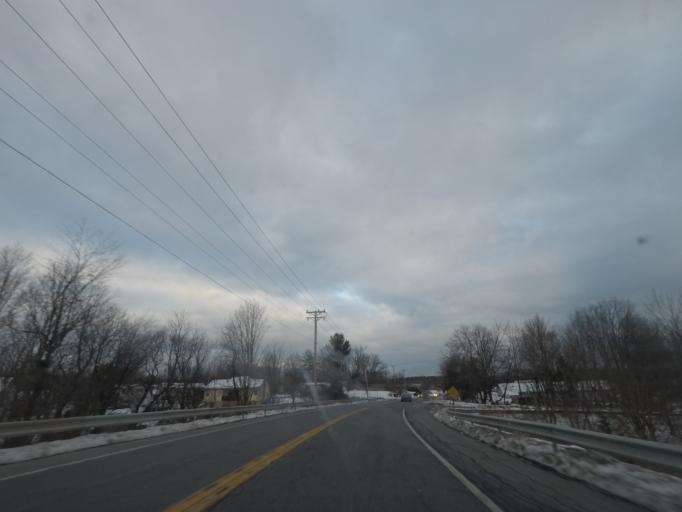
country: US
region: New York
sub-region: Ulster County
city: Plattekill
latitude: 41.6195
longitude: -74.0785
